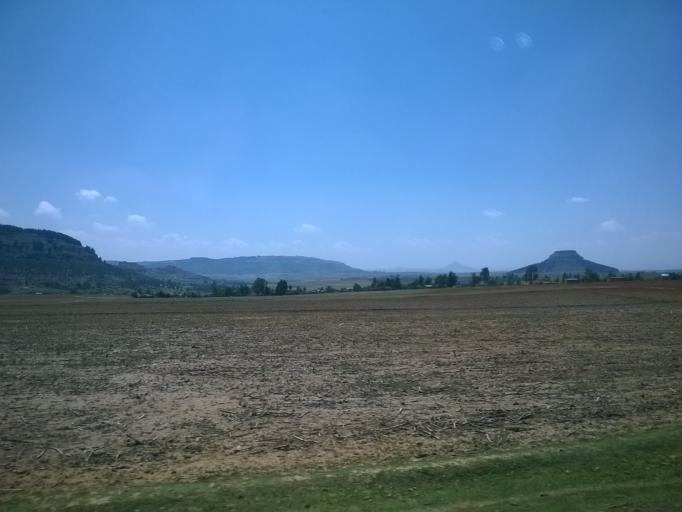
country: LS
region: Leribe
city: Maputsoe
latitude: -28.9687
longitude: 27.9673
